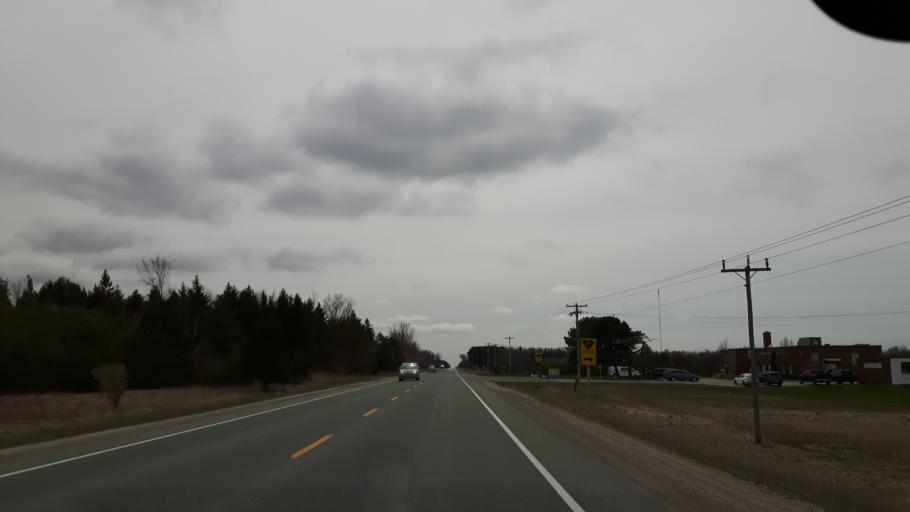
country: CA
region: Ontario
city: Goderich
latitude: 43.6891
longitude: -81.7057
